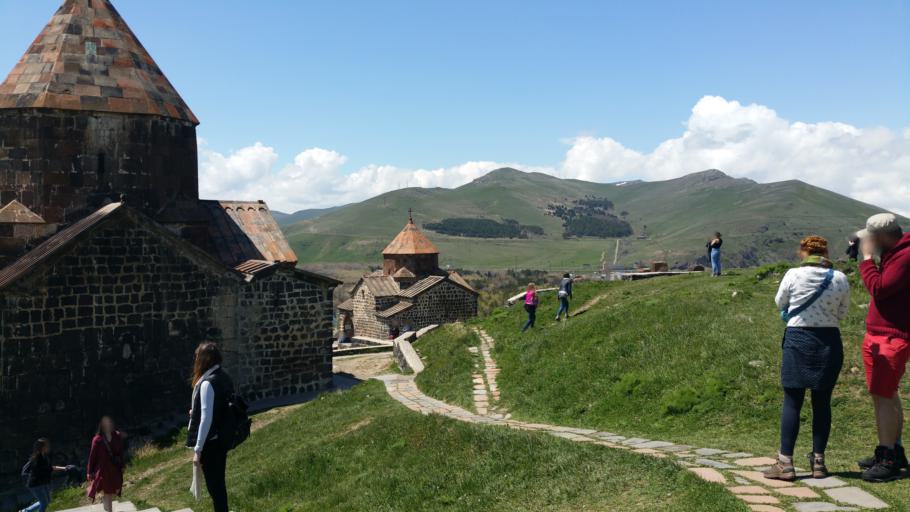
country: AM
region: Geghark'unik'i Marz
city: Sevan
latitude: 40.5640
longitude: 45.0113
